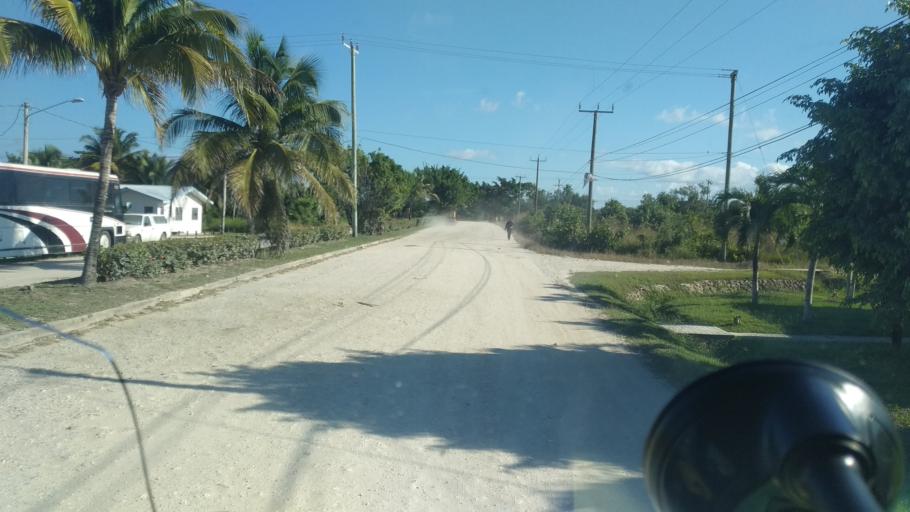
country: BZ
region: Belize
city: Belize City
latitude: 17.5728
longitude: -88.3384
